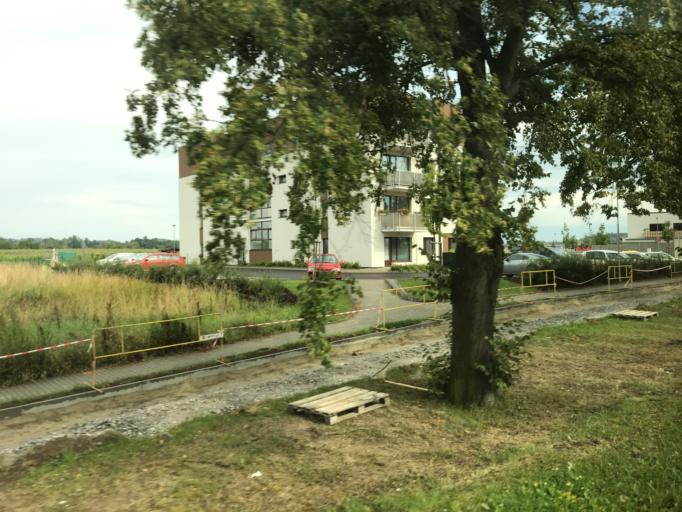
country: CZ
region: Jihocesky
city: Vcelna
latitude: 48.9408
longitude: 14.4643
